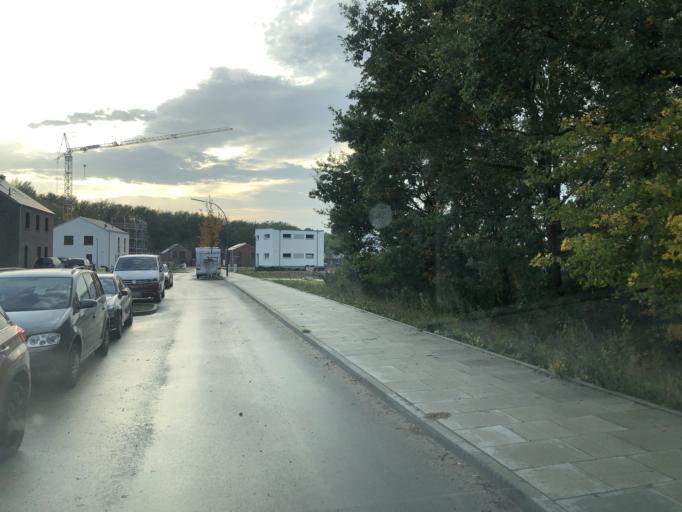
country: DE
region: Lower Saxony
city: Neu Wulmstorf
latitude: 53.4642
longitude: 9.8154
